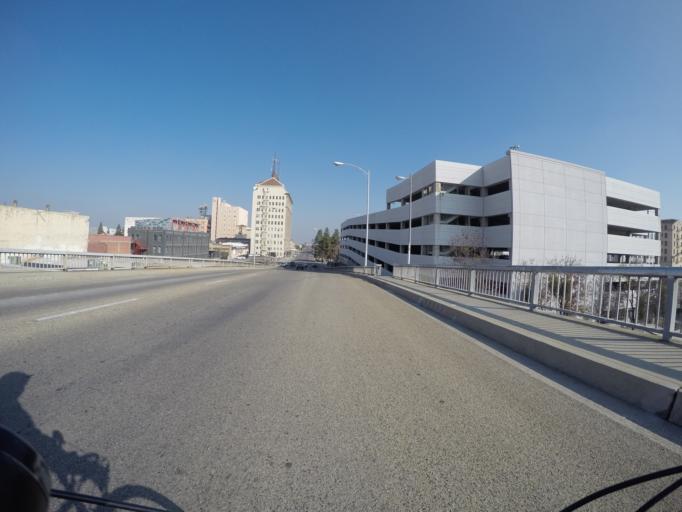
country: US
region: California
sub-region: Fresno County
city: Fresno
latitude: 36.7364
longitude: -119.7966
